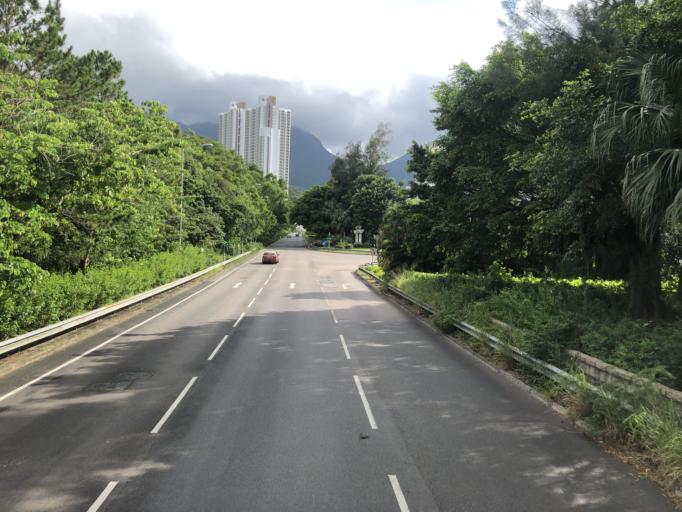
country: HK
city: Tai O
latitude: 22.2851
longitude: 113.9435
